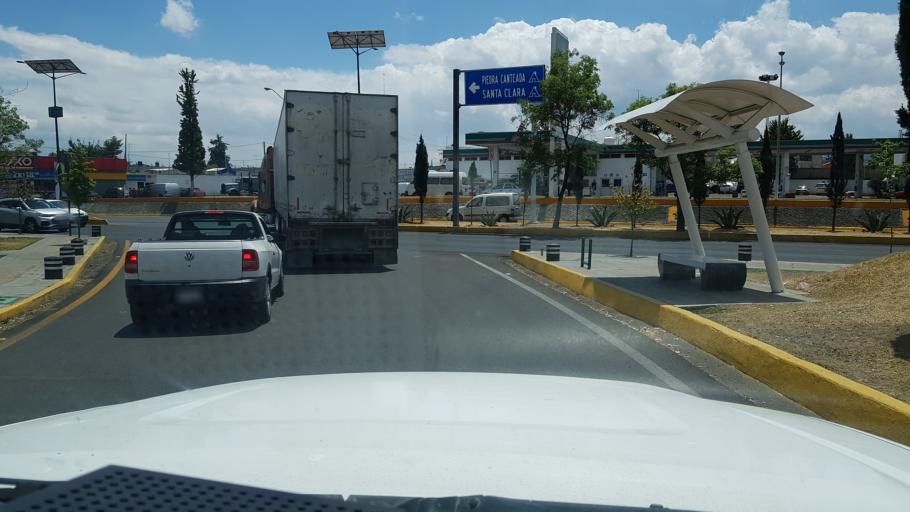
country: MX
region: Hidalgo
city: Calpulalpan
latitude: 19.5930
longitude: -98.5767
